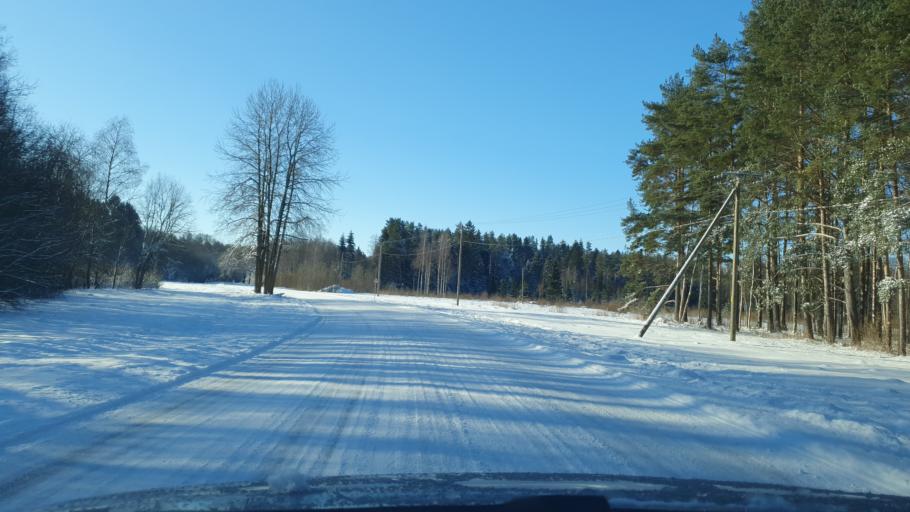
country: EE
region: Harju
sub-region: Kuusalu vald
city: Kuusalu
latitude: 59.4797
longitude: 25.4116
